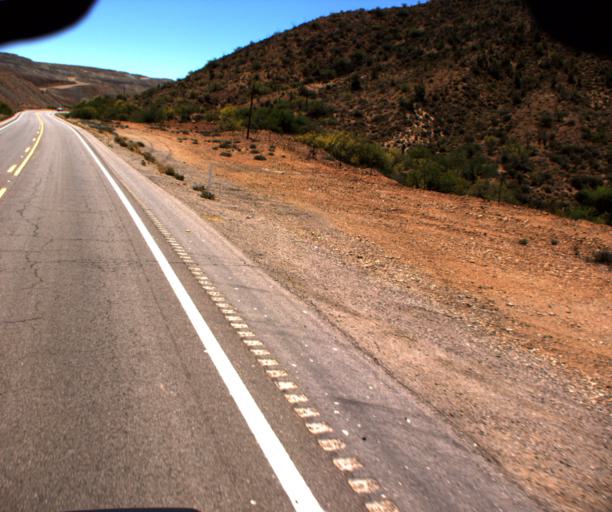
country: US
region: Arizona
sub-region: Pinal County
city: Kearny
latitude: 33.1649
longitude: -111.0041
